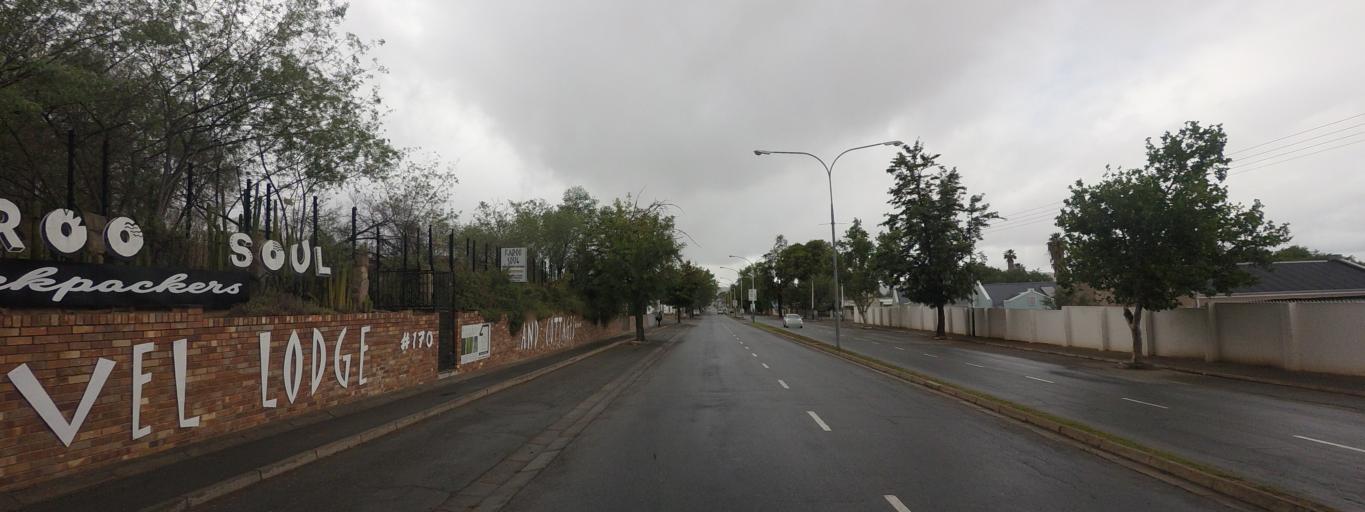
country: ZA
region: Western Cape
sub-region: Eden District Municipality
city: Oudtshoorn
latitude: -33.5974
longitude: 22.2052
